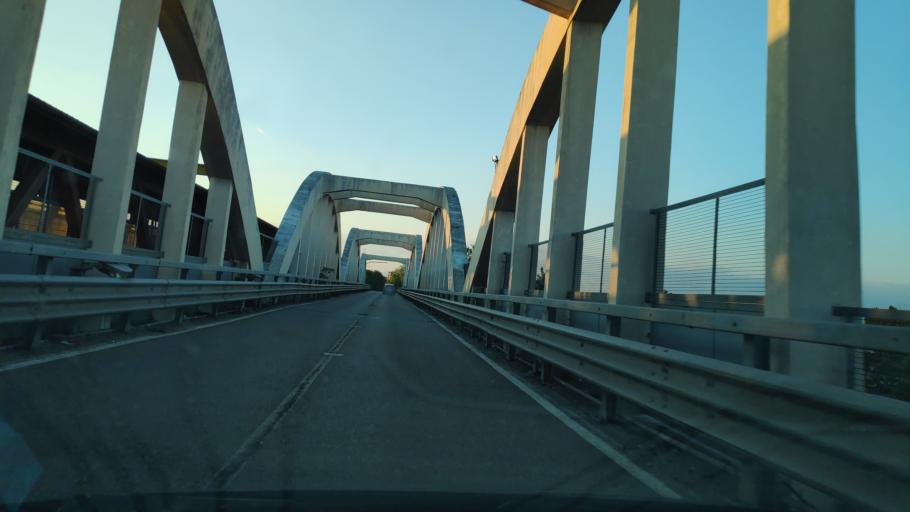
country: IT
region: Lombardy
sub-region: Citta metropolitana di Milano
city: Segrate
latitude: 45.4798
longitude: 9.3010
